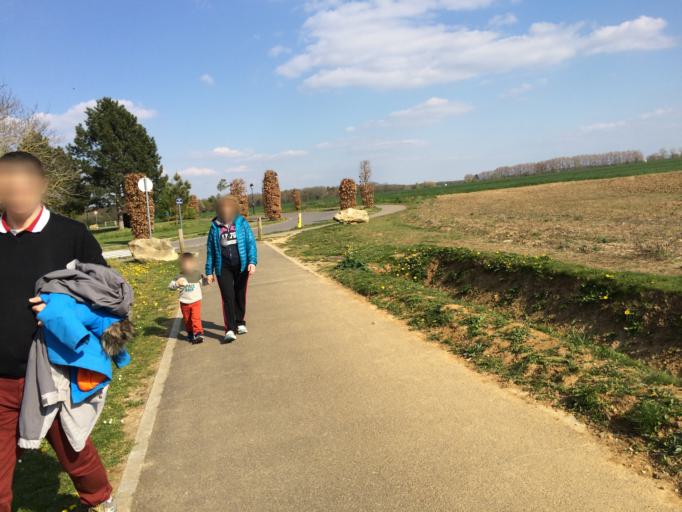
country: FR
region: Ile-de-France
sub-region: Departement des Yvelines
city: Jouy-en-Josas
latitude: 48.7513
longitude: 2.1839
